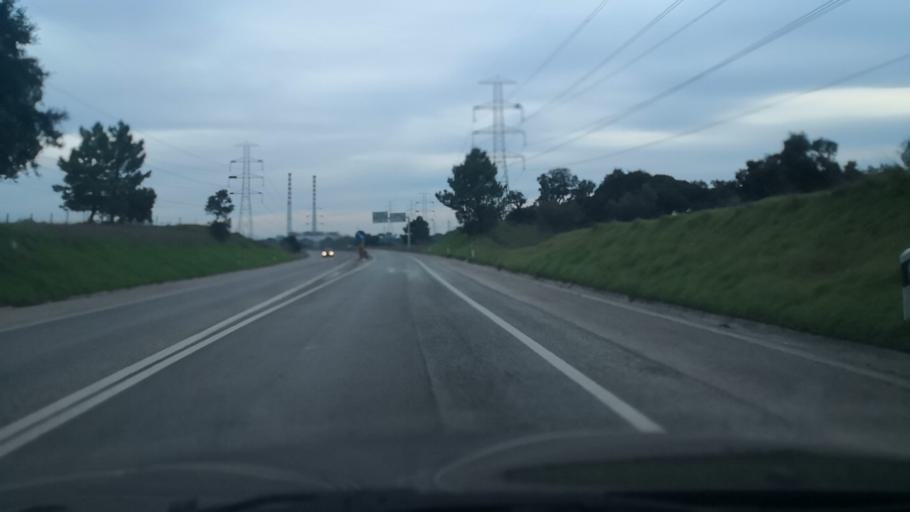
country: PT
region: Setubal
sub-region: Setubal
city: Setubal
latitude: 38.5282
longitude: -8.8437
